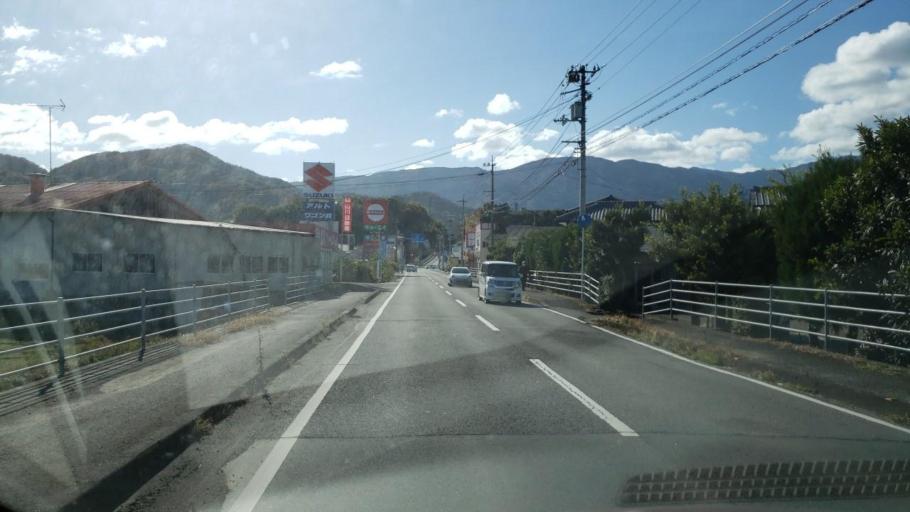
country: JP
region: Tokushima
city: Wakimachi
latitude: 34.0596
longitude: 134.2383
